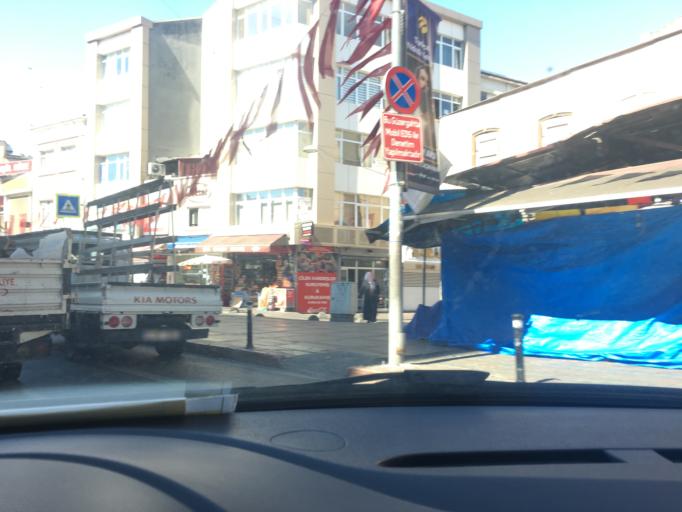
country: TR
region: Istanbul
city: Eminoenue
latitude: 41.0341
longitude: 28.9679
